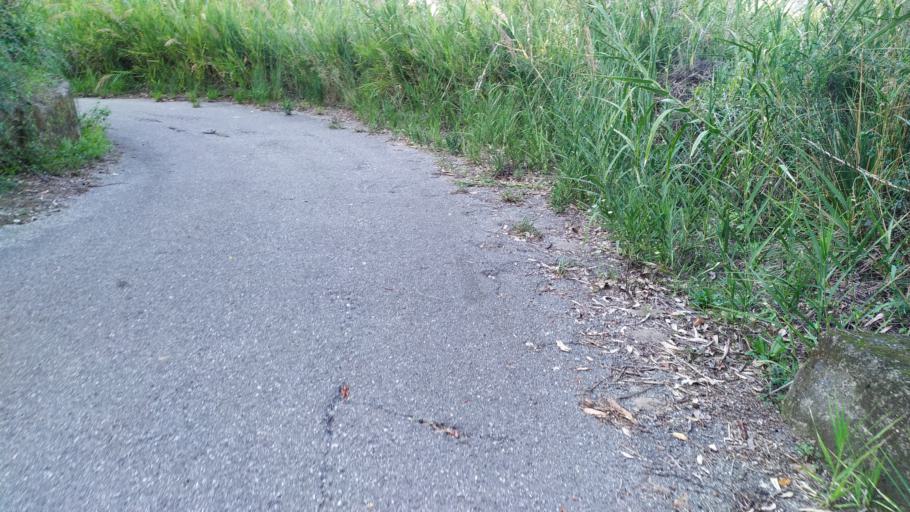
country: IT
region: Sicily
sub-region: Messina
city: Saponara Marittima
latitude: 38.2265
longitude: 15.4365
